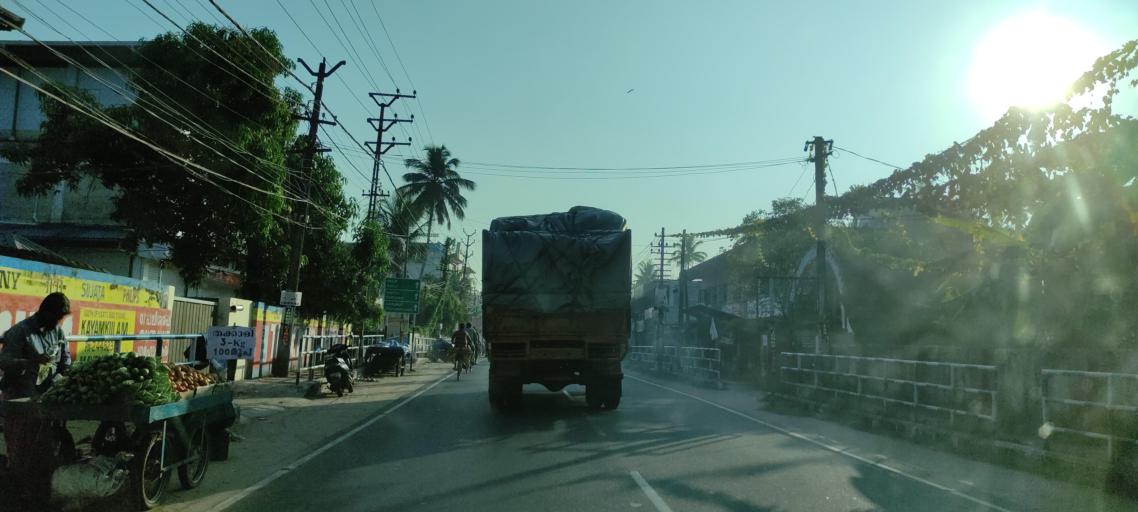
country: IN
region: Kerala
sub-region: Alappuzha
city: Kayankulam
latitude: 9.1752
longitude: 76.5038
